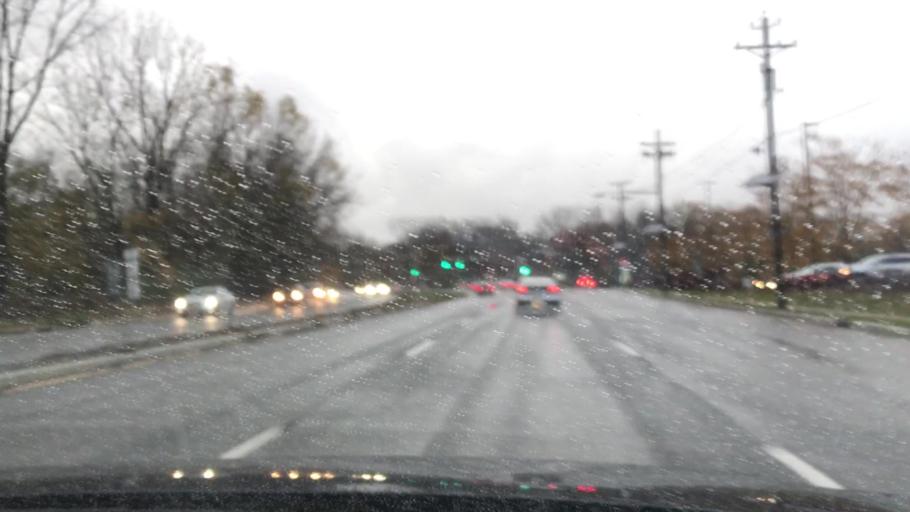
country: US
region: New Jersey
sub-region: Bergen County
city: Leonia
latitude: 40.8707
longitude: -74.0053
